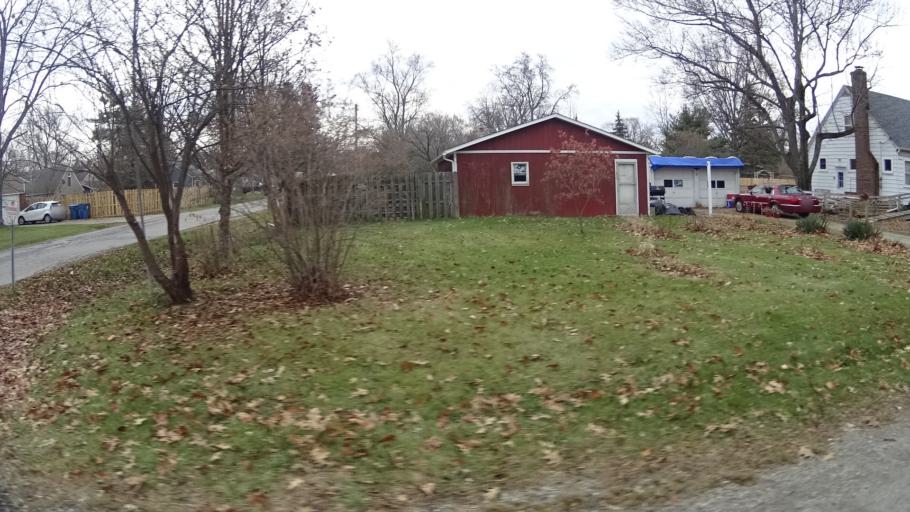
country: US
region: Ohio
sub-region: Cuyahoga County
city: Olmsted Falls
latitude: 41.3508
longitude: -81.8903
